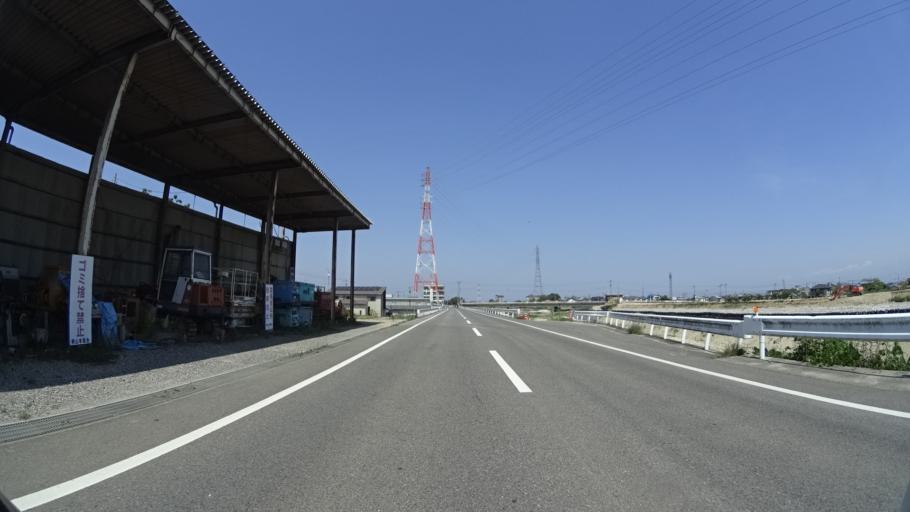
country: JP
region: Ehime
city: Hojo
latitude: 34.0373
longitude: 132.9750
